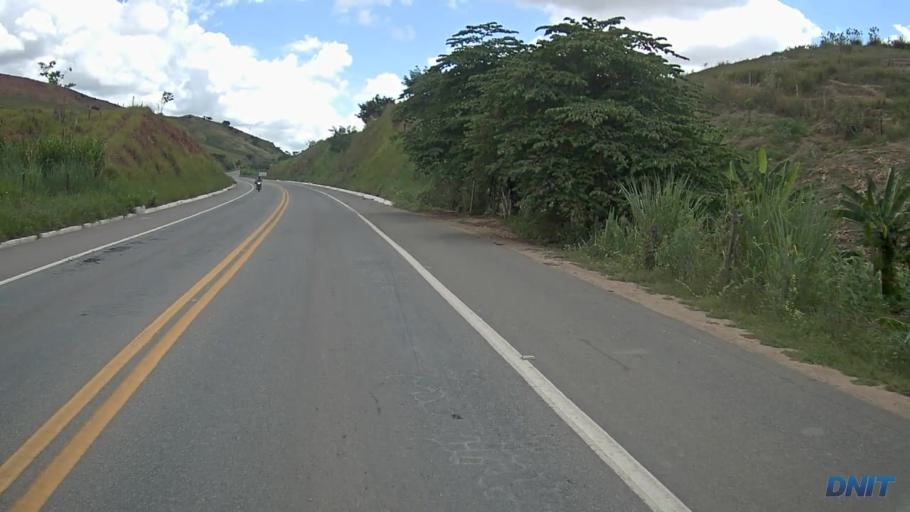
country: BR
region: Minas Gerais
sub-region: Governador Valadares
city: Governador Valadares
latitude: -18.8875
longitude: -42.0032
